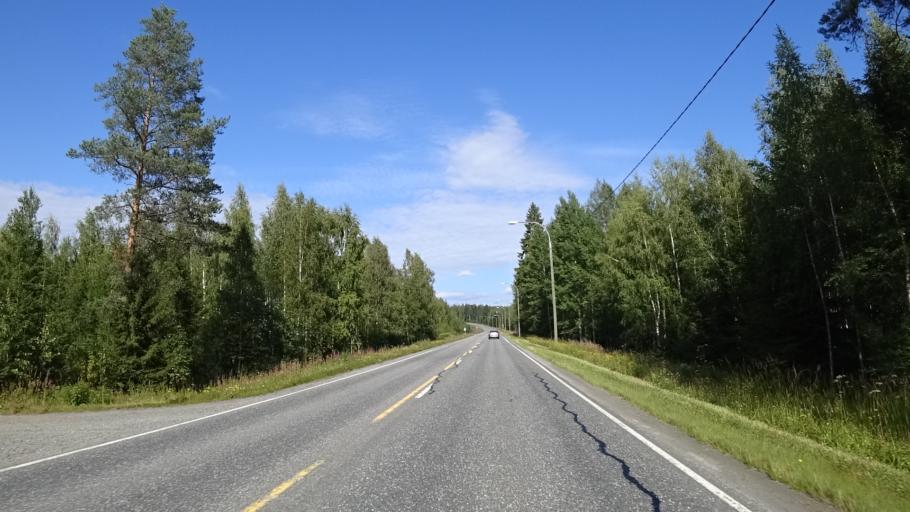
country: FI
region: North Karelia
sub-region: Joensuu
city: Eno
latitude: 62.7769
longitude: 30.0627
